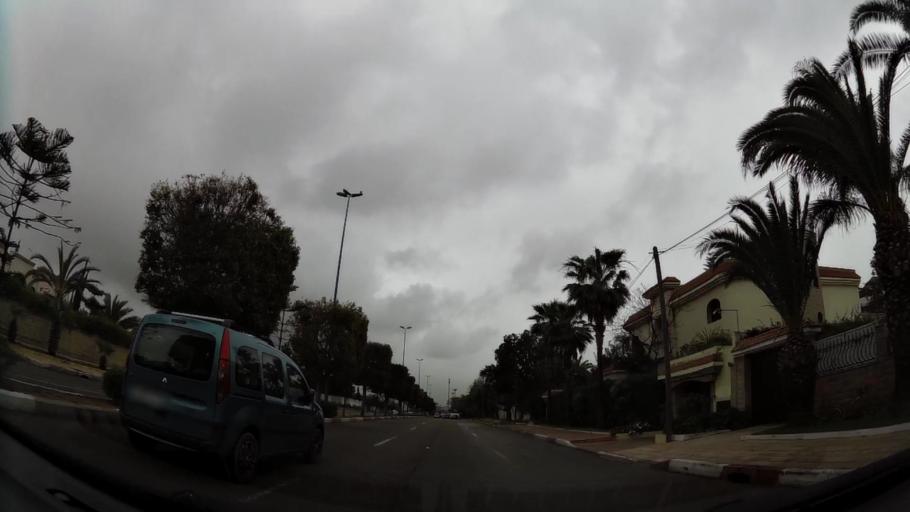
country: MA
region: Grand Casablanca
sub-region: Casablanca
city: Casablanca
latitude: 33.5424
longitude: -7.6216
